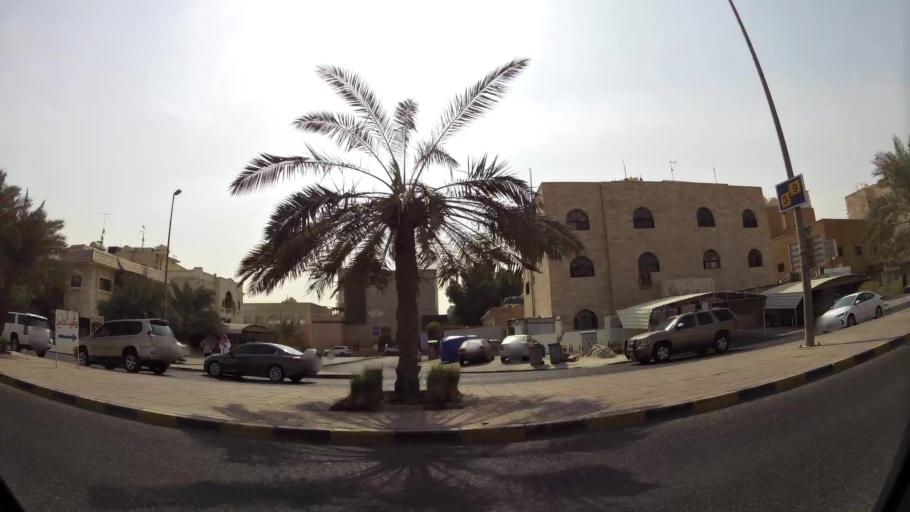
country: KW
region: Al Asimah
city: Ar Rabiyah
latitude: 29.3032
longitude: 47.8833
